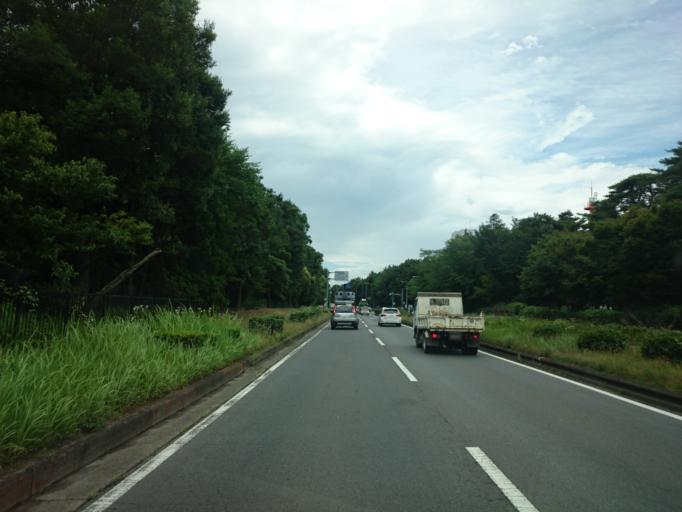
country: JP
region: Ibaraki
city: Tsukuba
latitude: 36.1244
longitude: 140.0747
